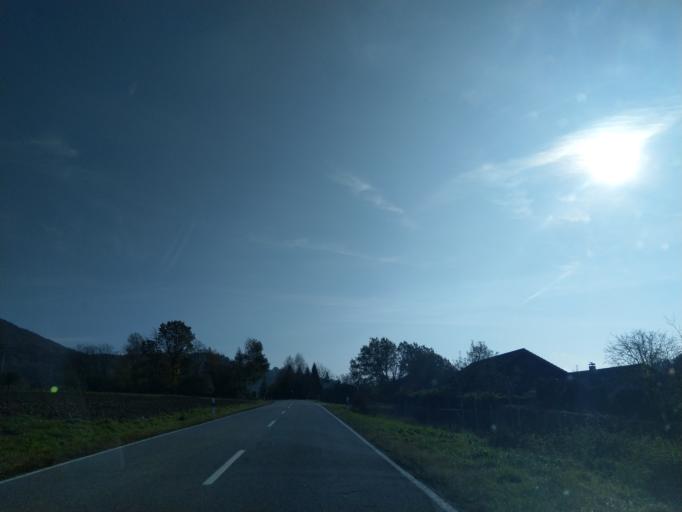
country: DE
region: Bavaria
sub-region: Lower Bavaria
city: Grattersdorf
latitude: 48.8086
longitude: 13.1408
